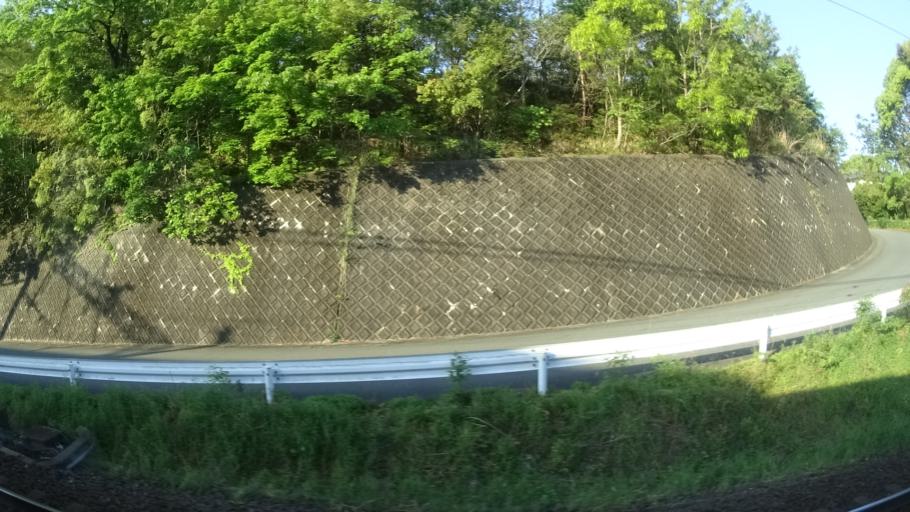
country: JP
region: Mie
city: Ise
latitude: 34.4777
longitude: 136.7247
